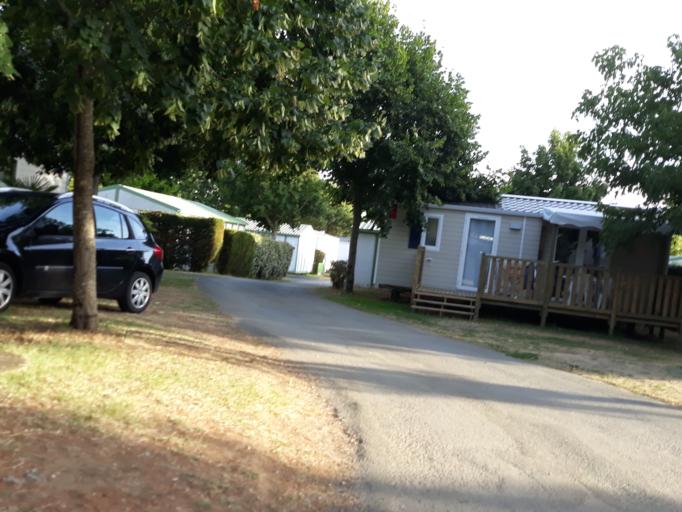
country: FR
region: Poitou-Charentes
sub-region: Departement de la Charente-Maritime
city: Saint-Laurent-de-la-Pree
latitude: 45.9883
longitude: -1.0525
